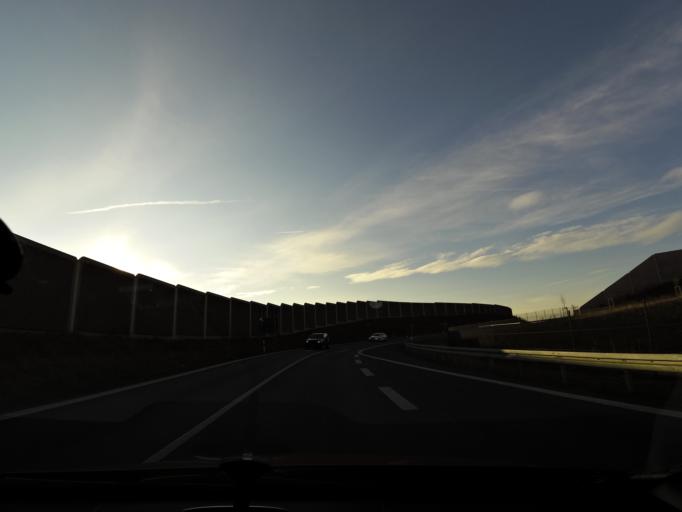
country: DE
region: Bavaria
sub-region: Regierungsbezirk Unterfranken
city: Kist
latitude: 49.7478
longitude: 9.8441
